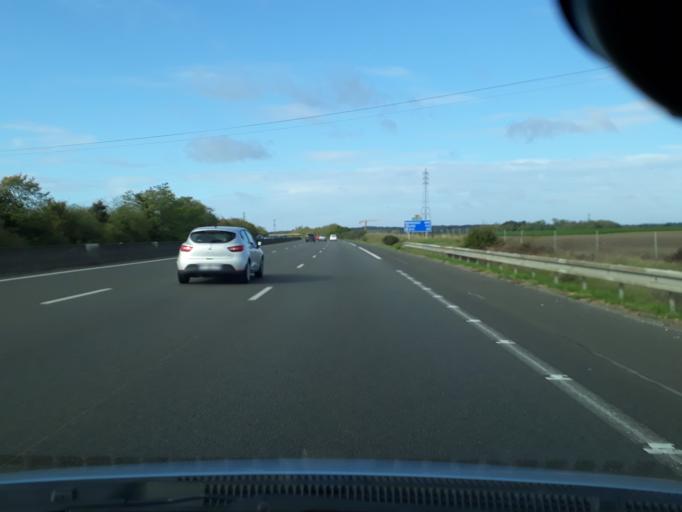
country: FR
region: Centre
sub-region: Departement du Loiret
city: La Chapelle-Saint-Mesmin
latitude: 47.9004
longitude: 1.8274
